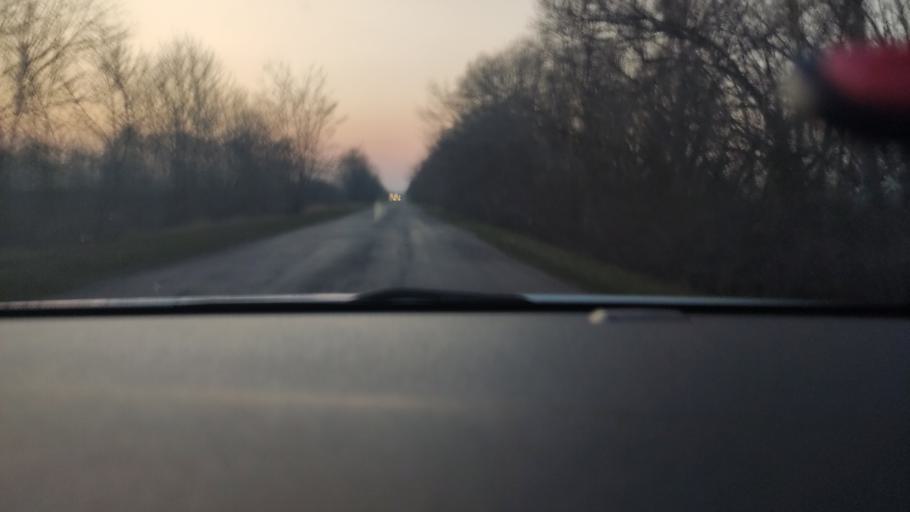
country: RU
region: Voronezj
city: Uryv-Pokrovka
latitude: 51.1405
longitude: 39.0764
